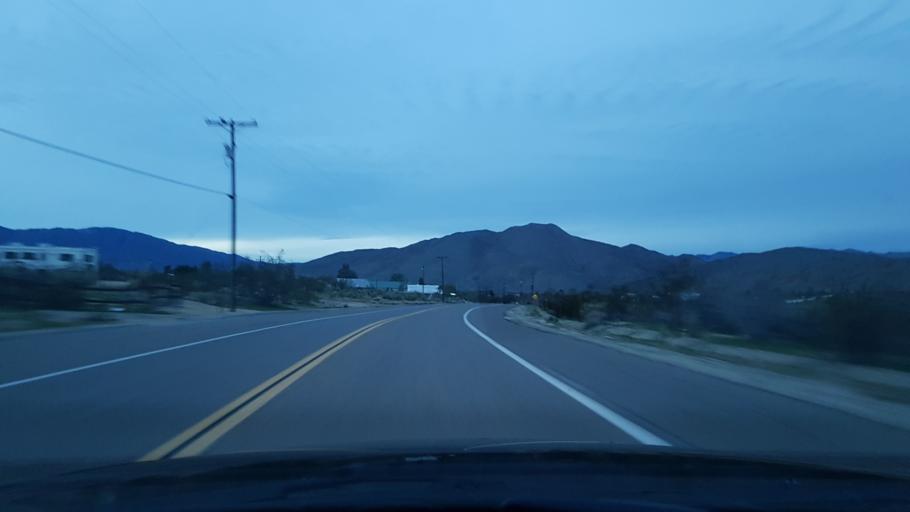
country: US
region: California
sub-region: San Diego County
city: Julian
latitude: 33.0751
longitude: -116.4359
